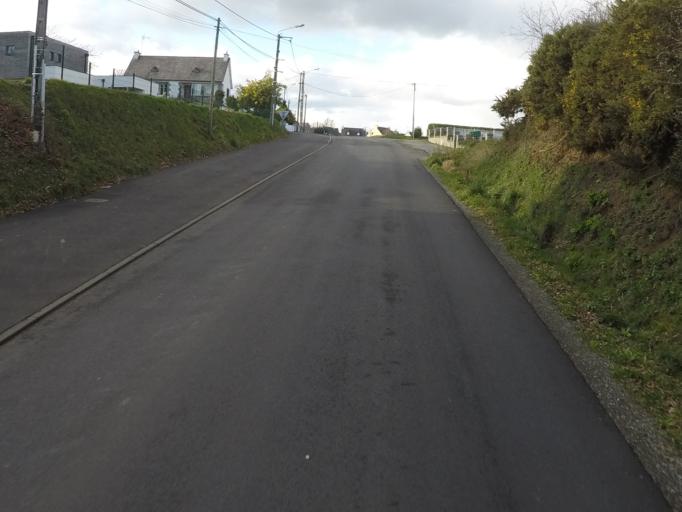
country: FR
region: Brittany
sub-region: Departement des Cotes-d'Armor
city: Plouagat
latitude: 48.5422
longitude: -2.9764
